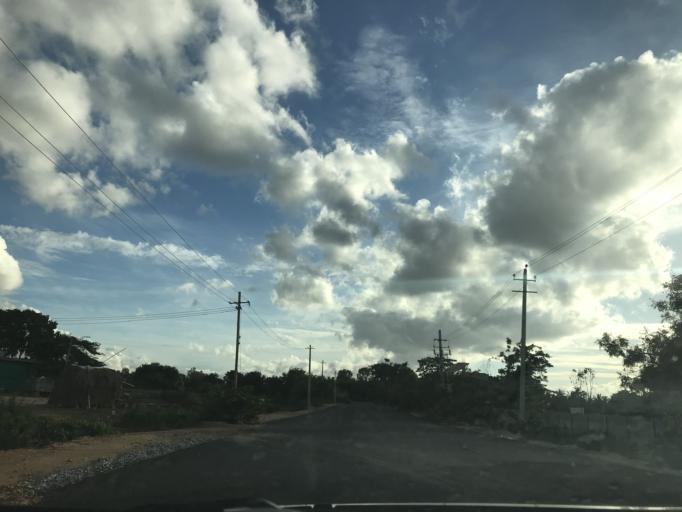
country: IN
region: Karnataka
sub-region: Bangalore Rural
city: Hoskote
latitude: 13.1368
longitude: 77.7357
